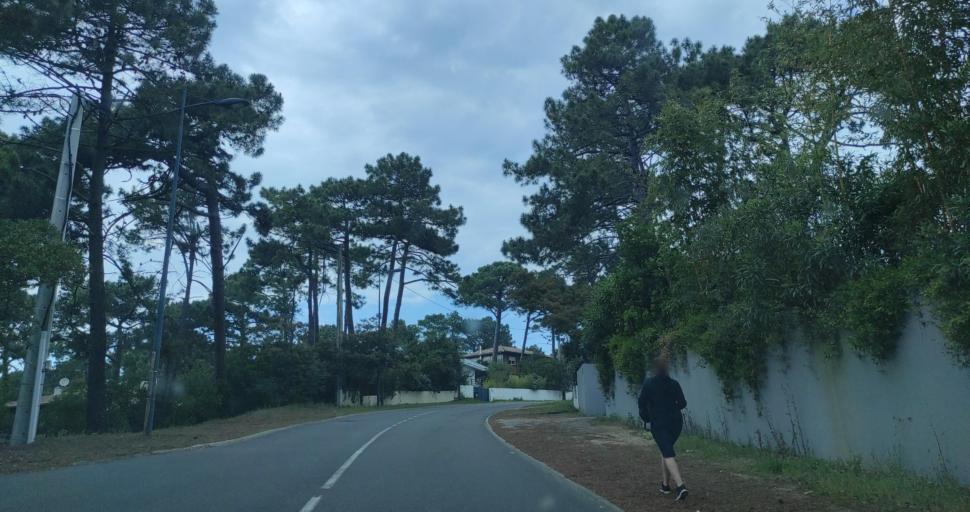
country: FR
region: Aquitaine
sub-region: Departement de la Gironde
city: Arcachon
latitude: 44.6680
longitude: -1.2432
